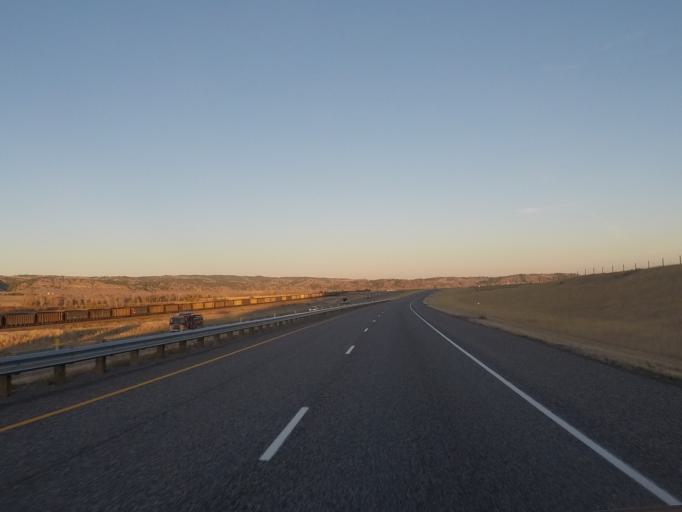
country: US
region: Montana
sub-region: Sweet Grass County
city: Big Timber
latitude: 45.7344
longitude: -109.7235
